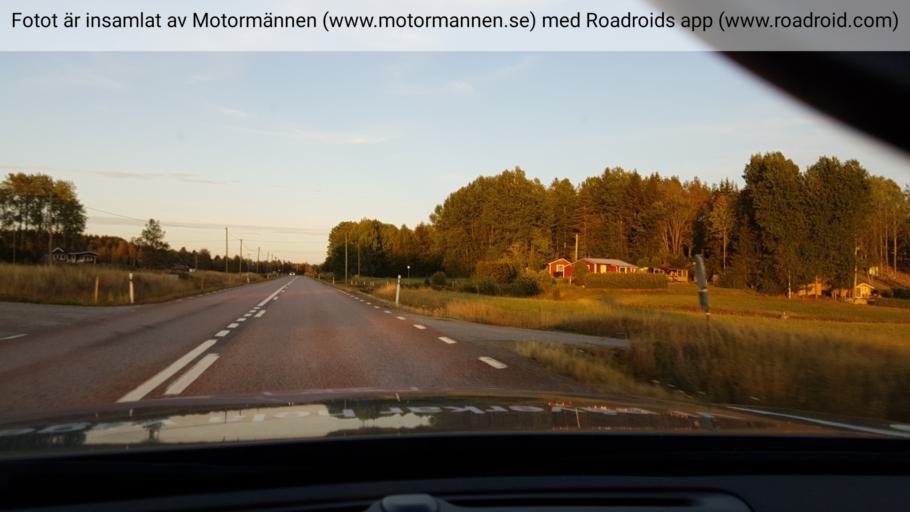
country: SE
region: OErebro
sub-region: Karlskoga Kommun
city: Karlskoga
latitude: 59.3933
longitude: 14.4531
